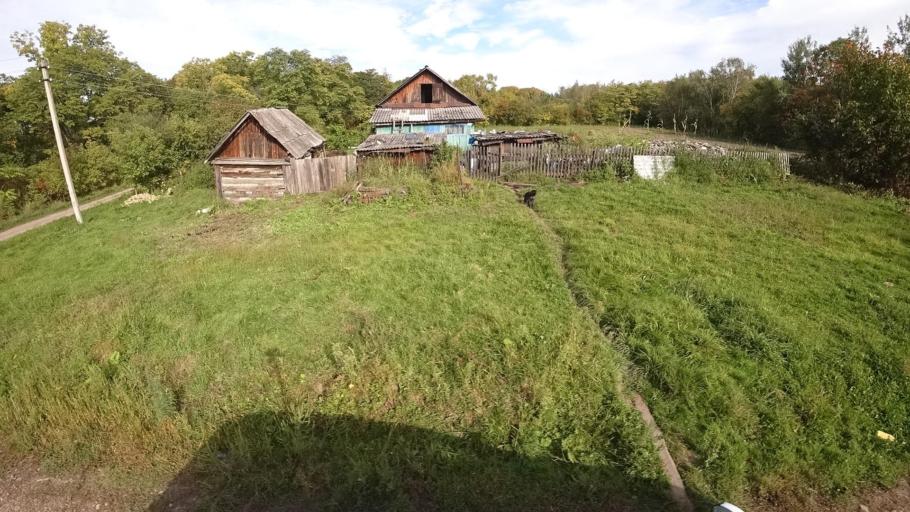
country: RU
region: Primorskiy
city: Dostoyevka
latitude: 44.2932
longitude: 133.4487
